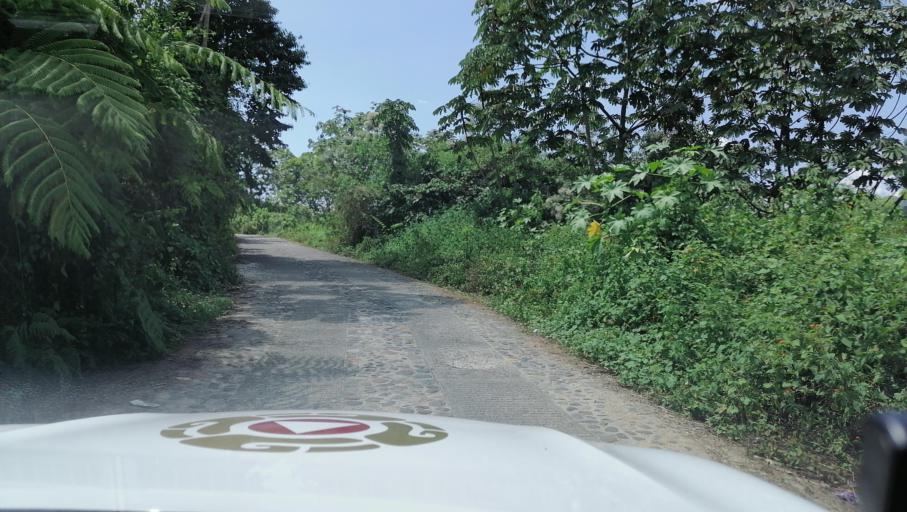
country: MX
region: Chiapas
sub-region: Tapachula
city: Canton Villaflor
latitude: 15.1373
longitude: -92.2875
